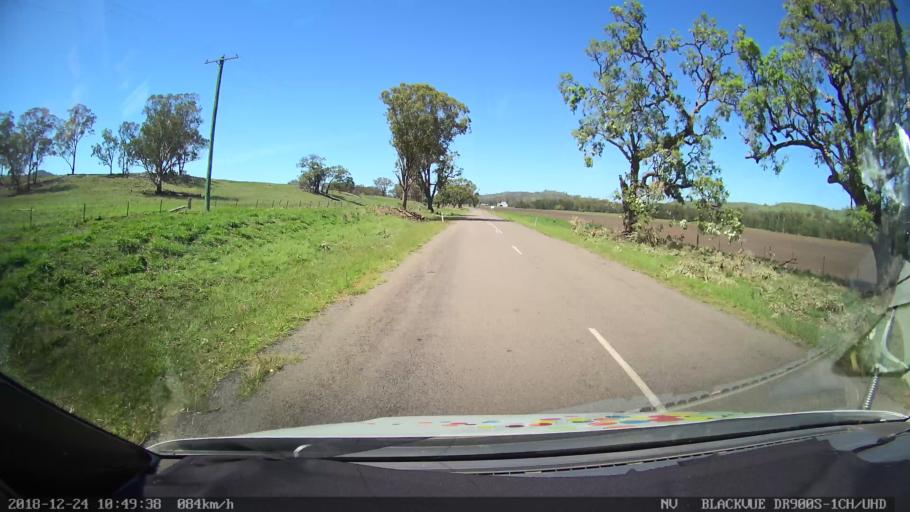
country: AU
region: New South Wales
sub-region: Upper Hunter Shire
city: Merriwa
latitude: -31.9501
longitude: 150.4264
